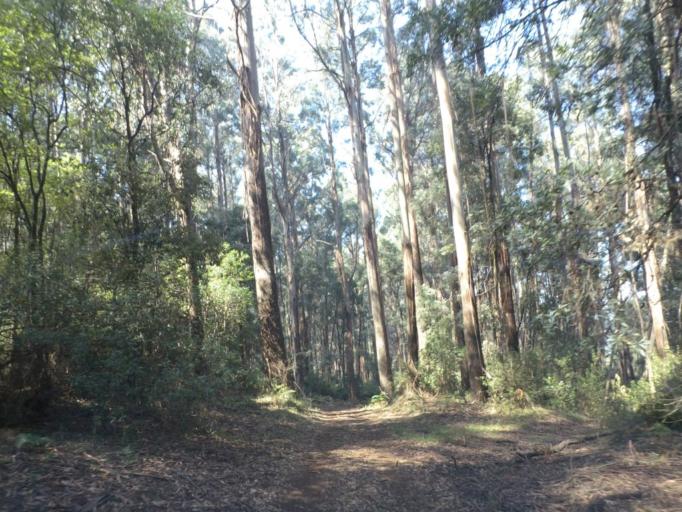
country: AU
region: Victoria
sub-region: Yarra Ranges
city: Healesville
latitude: -37.5612
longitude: 145.6131
